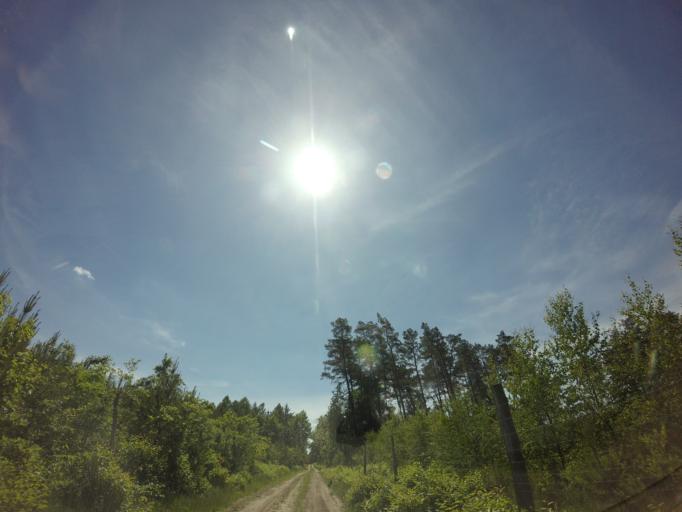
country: PL
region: West Pomeranian Voivodeship
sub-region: Powiat choszczenski
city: Drawno
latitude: 53.2556
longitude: 15.7485
